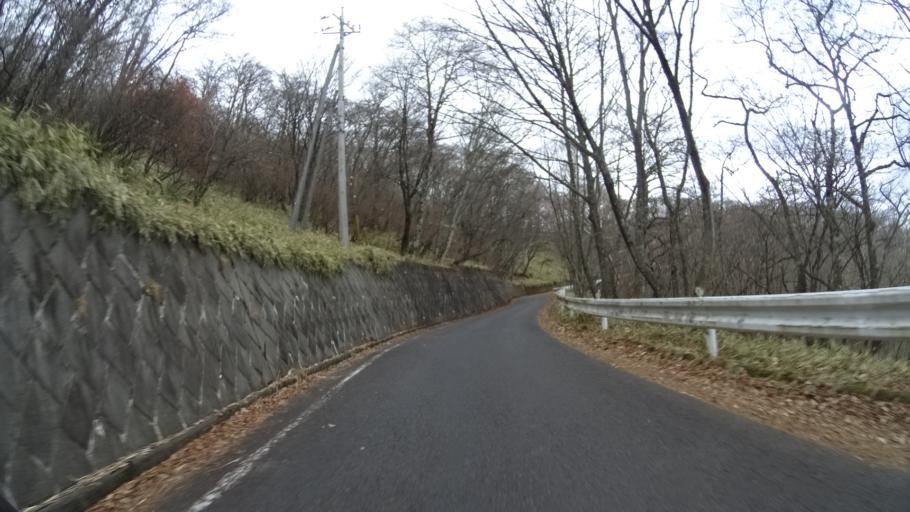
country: JP
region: Gunma
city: Omamacho-omama
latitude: 36.5233
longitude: 139.1785
